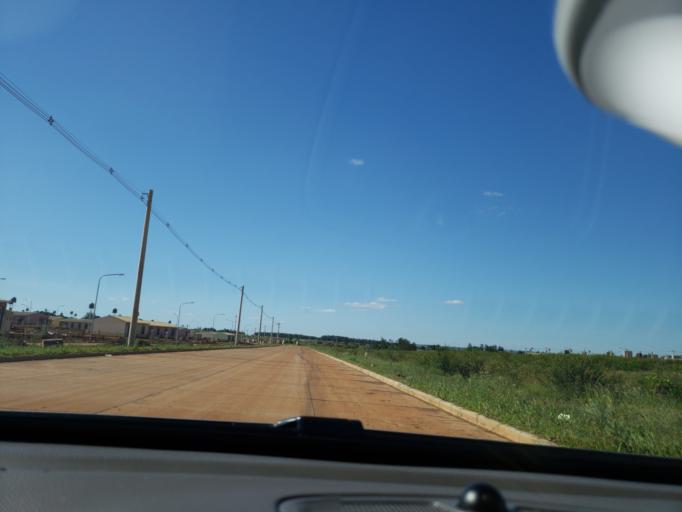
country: AR
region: Misiones
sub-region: Departamento de Capital
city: Posadas
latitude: -27.4022
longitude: -55.9887
